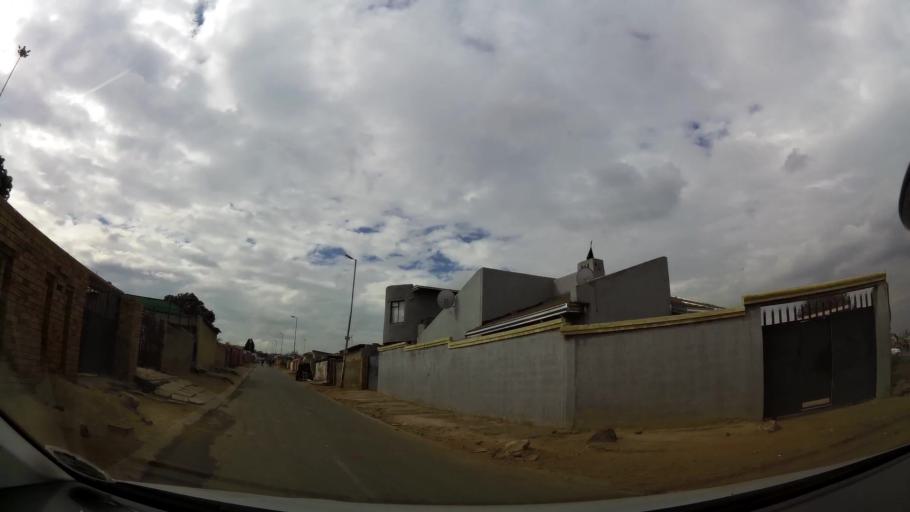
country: ZA
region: Gauteng
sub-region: City of Johannesburg Metropolitan Municipality
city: Soweto
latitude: -26.2821
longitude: 27.8555
